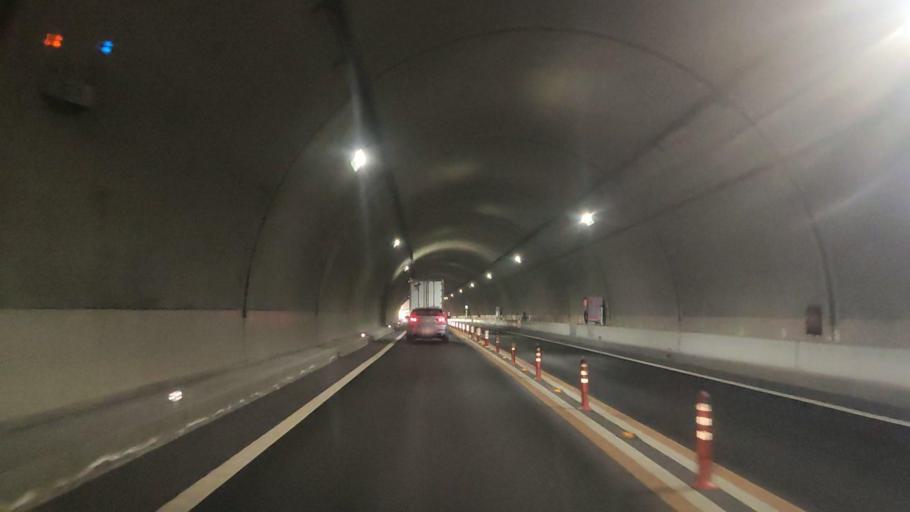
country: JP
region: Fukuoka
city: Kanda
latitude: 33.7872
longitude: 130.9710
